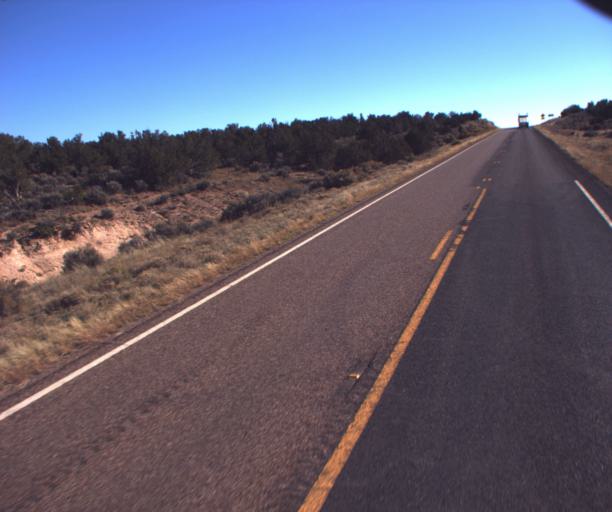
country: US
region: Arizona
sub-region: Apache County
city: Ganado
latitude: 35.4862
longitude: -109.5291
